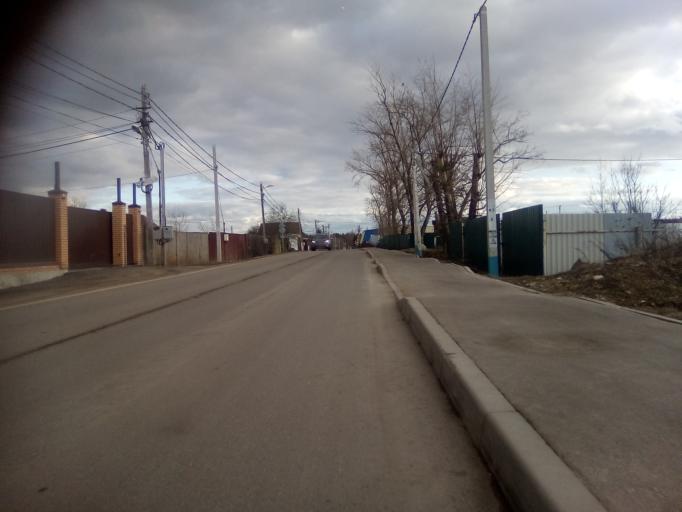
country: RU
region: Moskovskaya
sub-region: Leninskiy Rayon
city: Vnukovo
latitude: 55.5942
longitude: 37.3192
